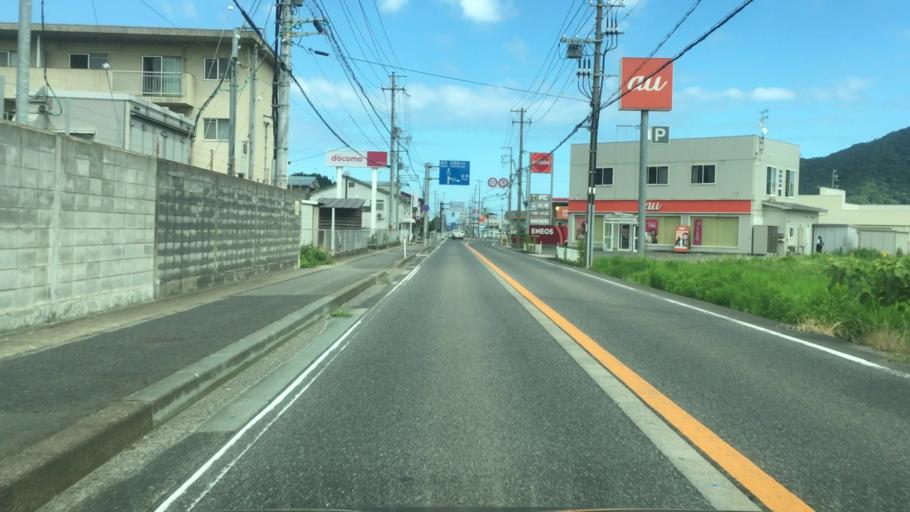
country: JP
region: Tottori
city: Tottori
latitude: 35.6132
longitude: 134.4676
